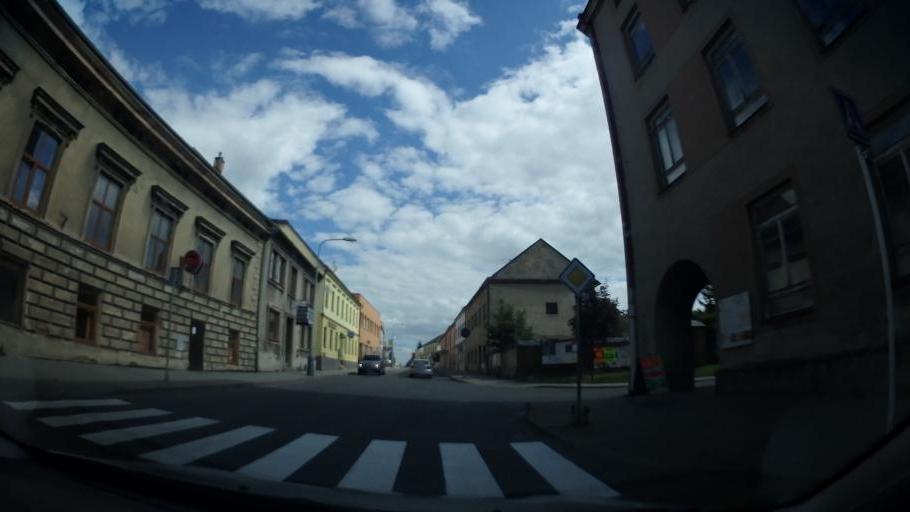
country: CZ
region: Pardubicky
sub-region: Okres Svitavy
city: Moravska Trebova
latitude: 49.7565
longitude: 16.6603
